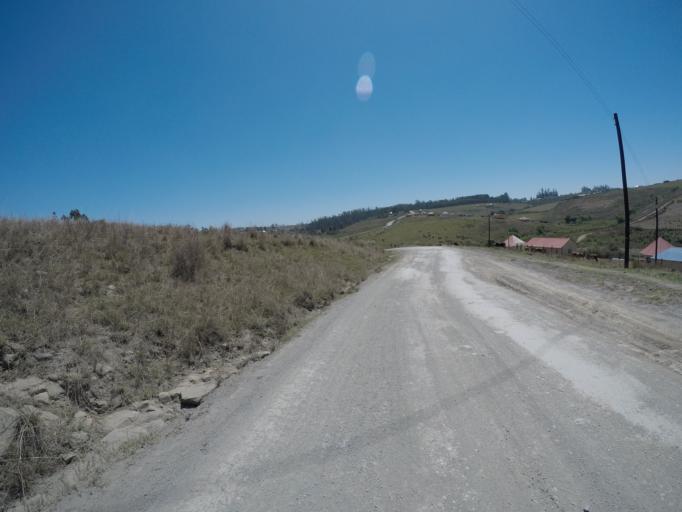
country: ZA
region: Eastern Cape
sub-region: OR Tambo District Municipality
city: Libode
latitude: -31.9688
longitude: 29.0264
